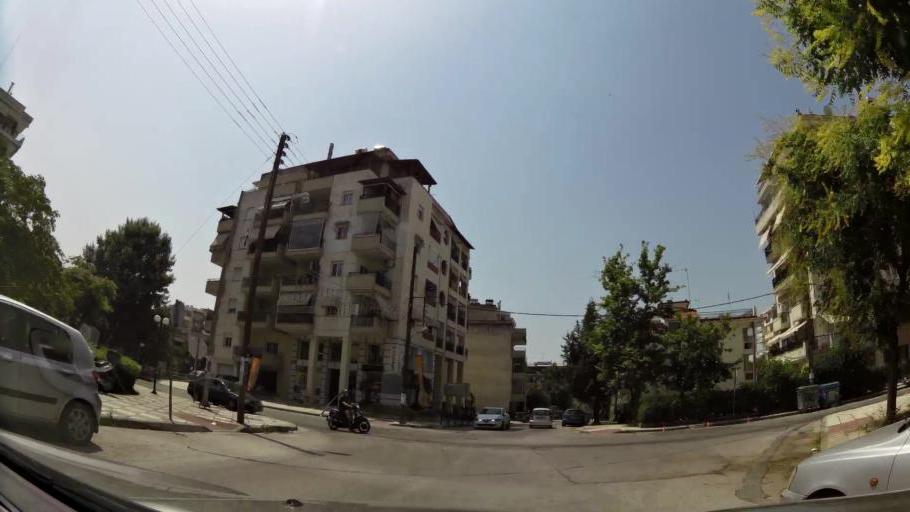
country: GR
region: Central Macedonia
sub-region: Nomos Thessalonikis
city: Evosmos
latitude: 40.6735
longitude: 22.9084
